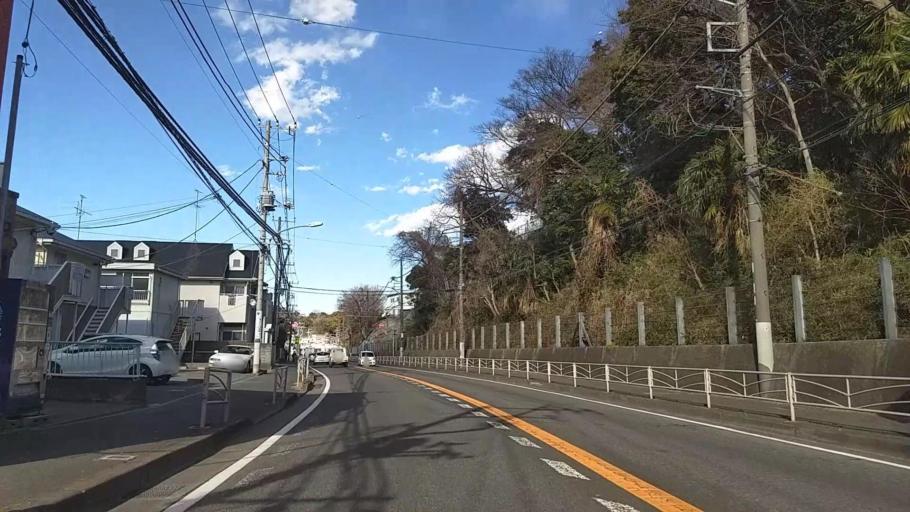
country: JP
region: Kanagawa
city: Yokohama
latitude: 35.3644
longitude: 139.6309
